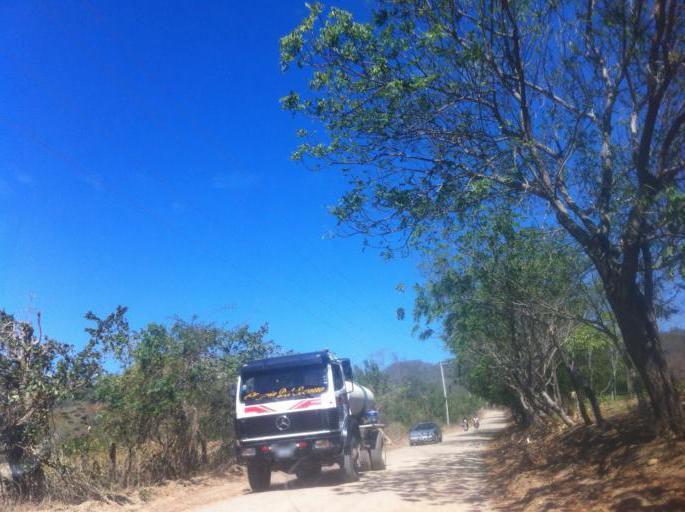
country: NI
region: Rivas
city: Tola
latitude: 11.3987
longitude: -85.9981
